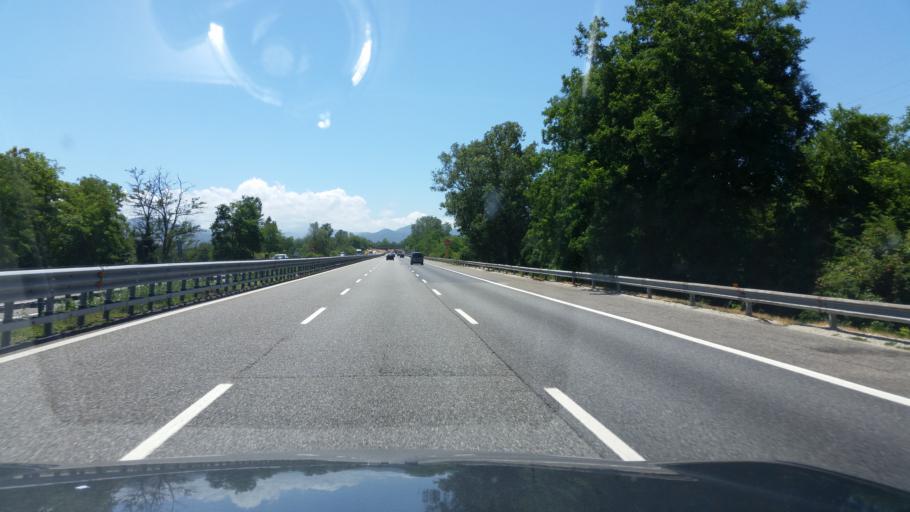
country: IT
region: Piedmont
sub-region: Provincia di Alessandria
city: Silvano d'Orba
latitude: 44.6984
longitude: 8.6666
